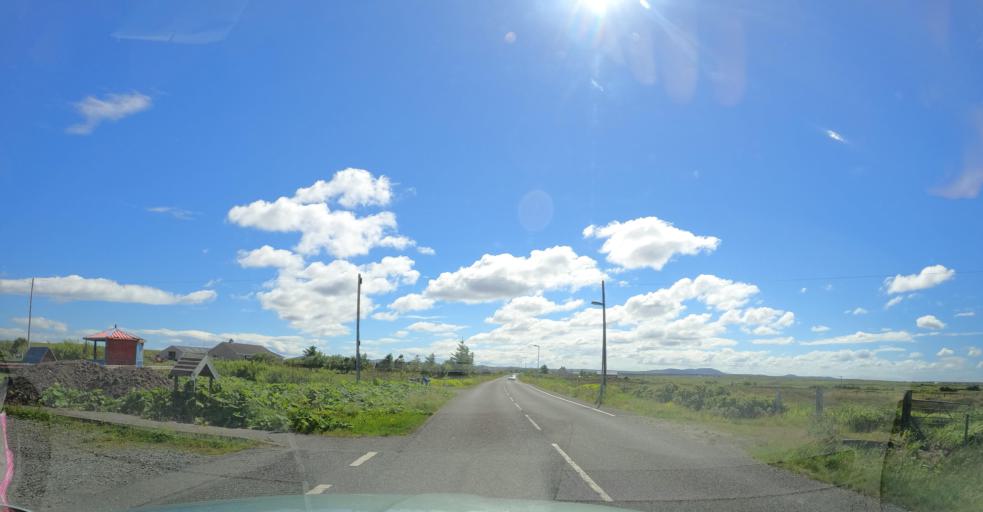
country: GB
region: Scotland
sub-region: Eilean Siar
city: Isle of Lewis
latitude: 58.3639
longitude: -6.5083
